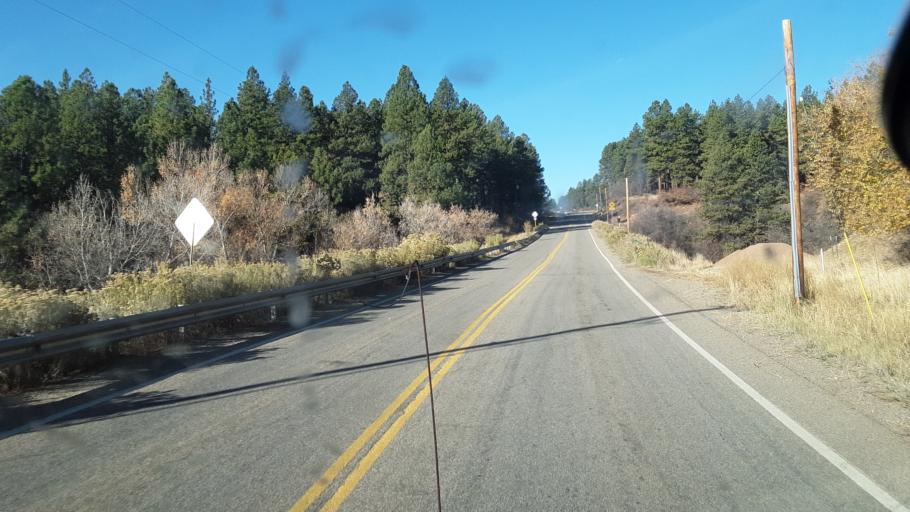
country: US
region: Colorado
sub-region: La Plata County
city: Durango
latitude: 37.3115
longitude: -107.7788
